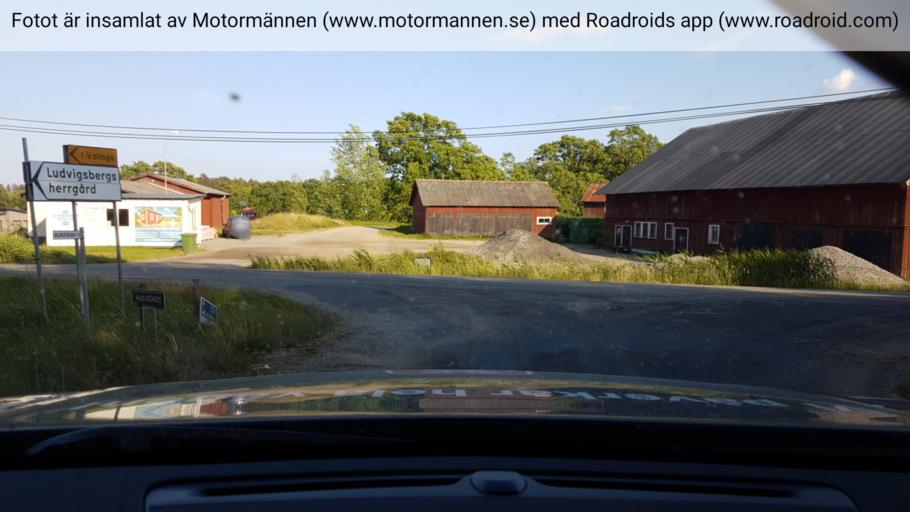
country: SE
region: Stockholm
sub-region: Haninge Kommun
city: Jordbro
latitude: 59.0075
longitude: 18.1236
